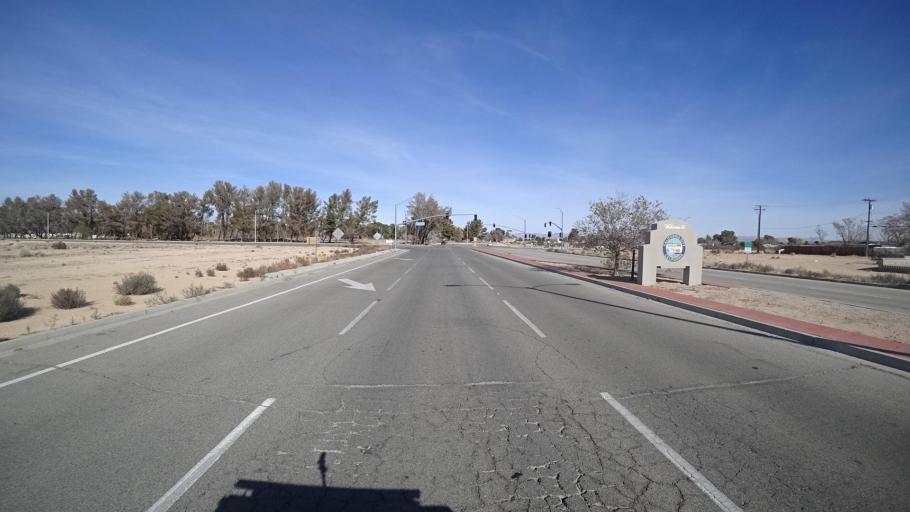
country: US
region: California
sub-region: Kern County
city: California City
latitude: 35.1252
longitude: -117.9410
